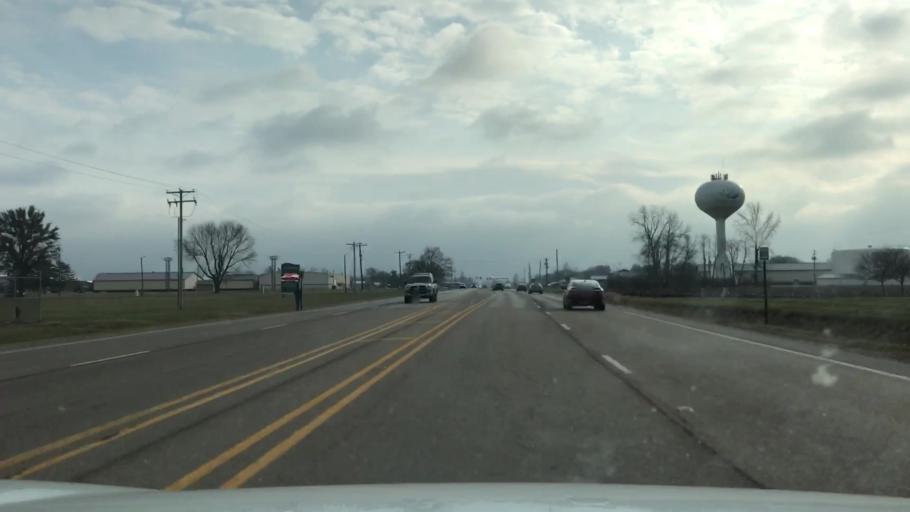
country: US
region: Illinois
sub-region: Madison County
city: Bethalto
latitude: 38.8926
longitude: -90.0593
